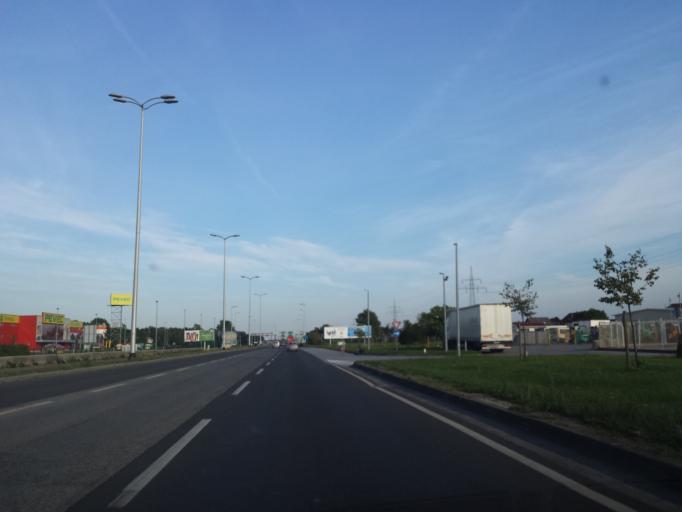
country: HR
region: Grad Zagreb
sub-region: Sesvete
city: Sesvete
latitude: 45.8037
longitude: 16.1148
